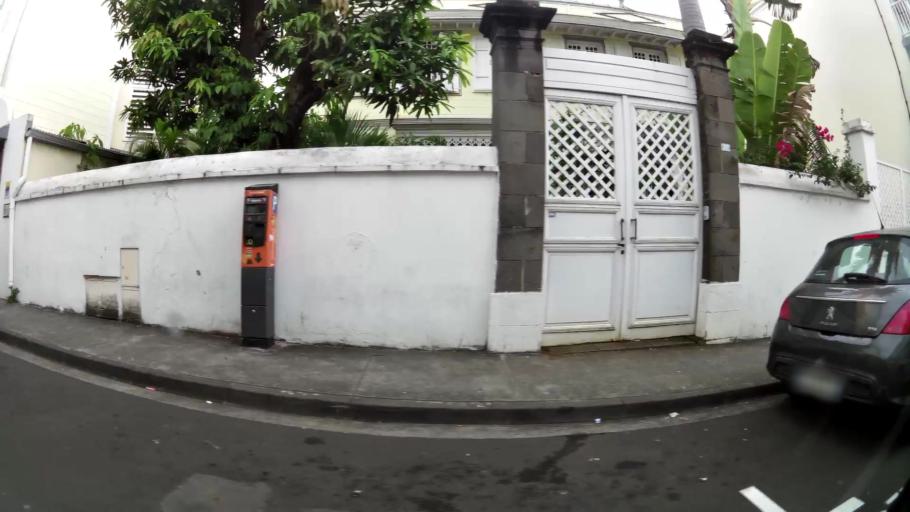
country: RE
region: Reunion
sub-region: Reunion
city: Saint-Denis
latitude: -20.8779
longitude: 55.4525
